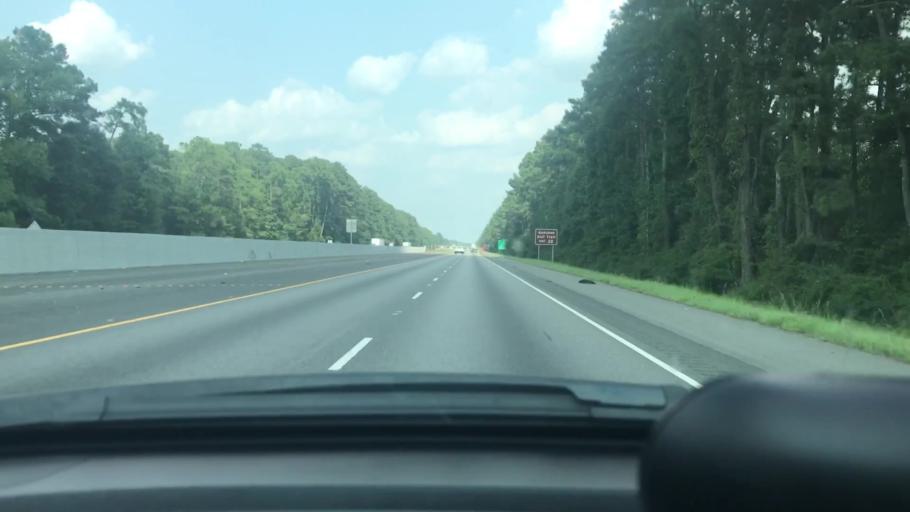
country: US
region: Louisiana
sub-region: Livingston Parish
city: Albany
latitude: 30.4764
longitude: -90.5944
